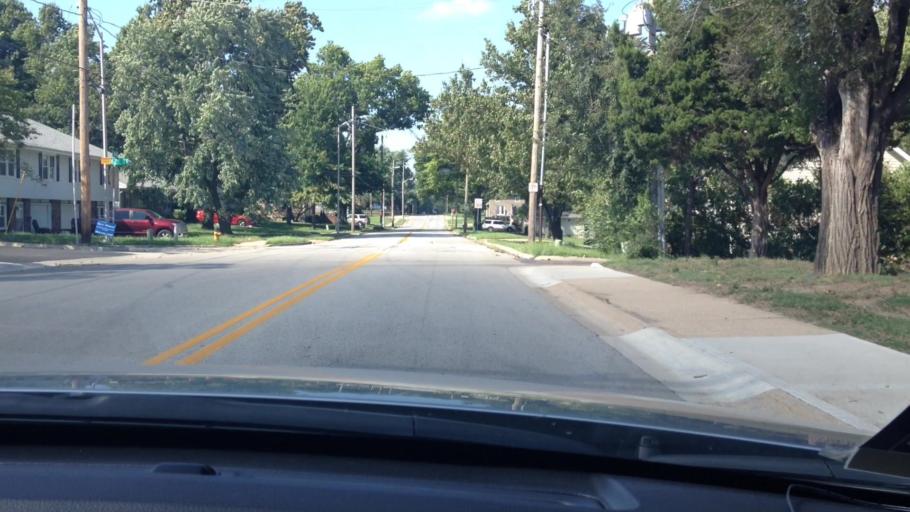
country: US
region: Kansas
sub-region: Johnson County
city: Shawnee
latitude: 39.0163
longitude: -94.7308
